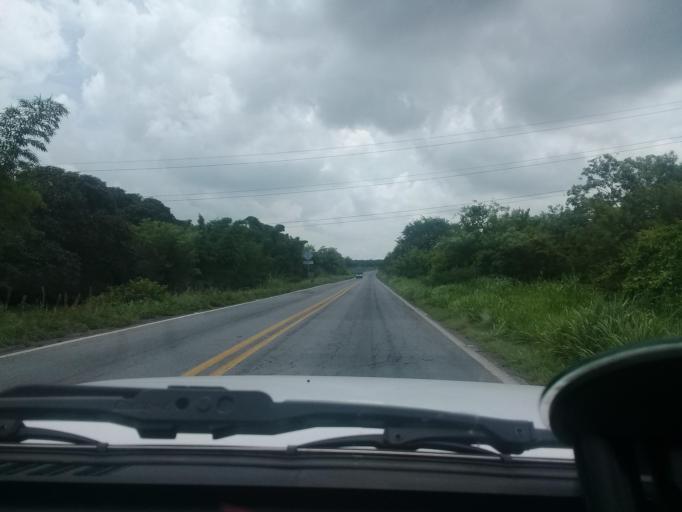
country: MX
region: Veracruz
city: Paso de Ovejas
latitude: 19.2917
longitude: -96.4559
